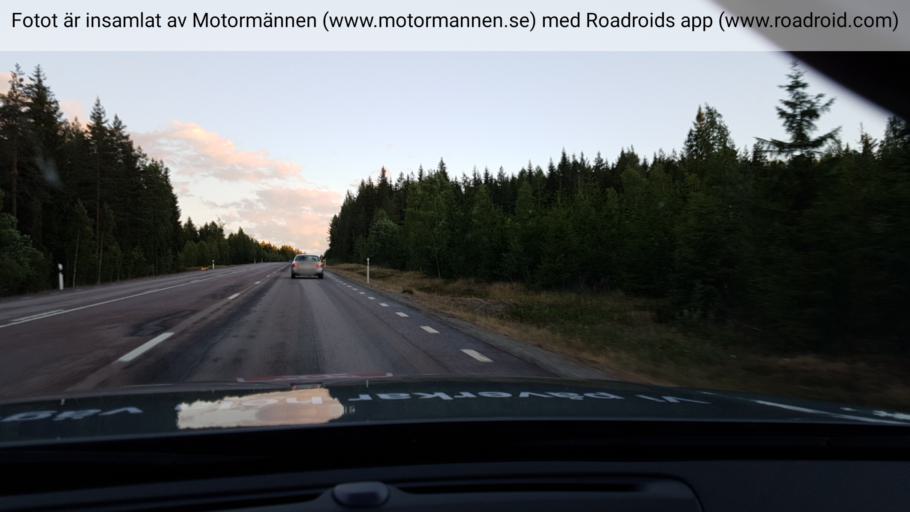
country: SE
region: Vaestmanland
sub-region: Fagersta Kommun
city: Fagersta
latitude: 59.9532
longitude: 15.7540
